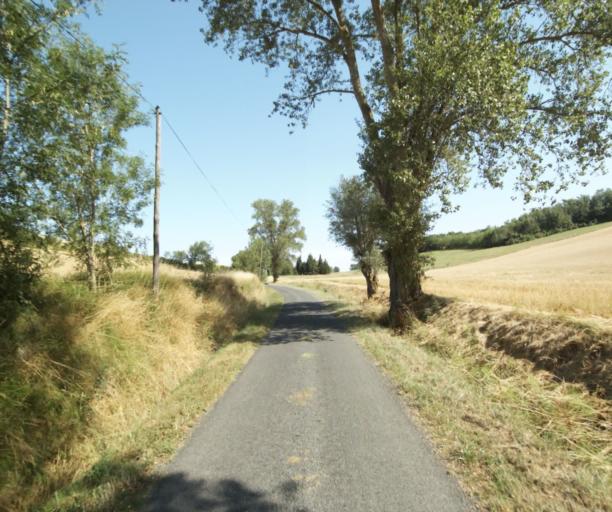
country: FR
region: Midi-Pyrenees
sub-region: Departement de la Haute-Garonne
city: Saint-Felix-Lauragais
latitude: 43.4319
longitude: 1.8483
